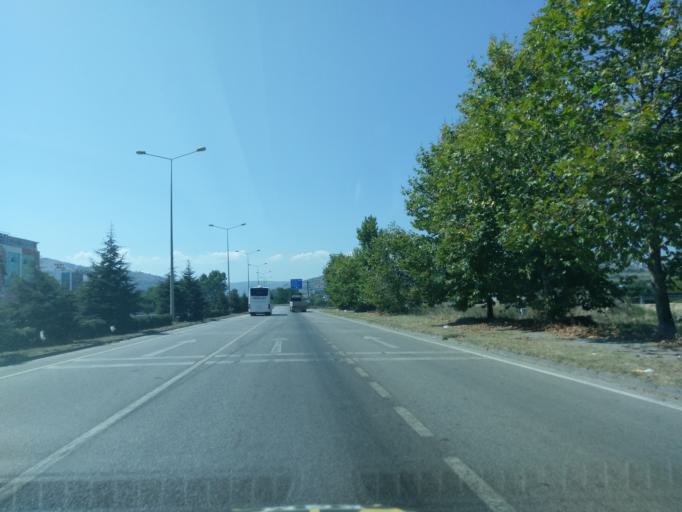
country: TR
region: Samsun
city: Samsun
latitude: 41.2554
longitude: 36.3217
